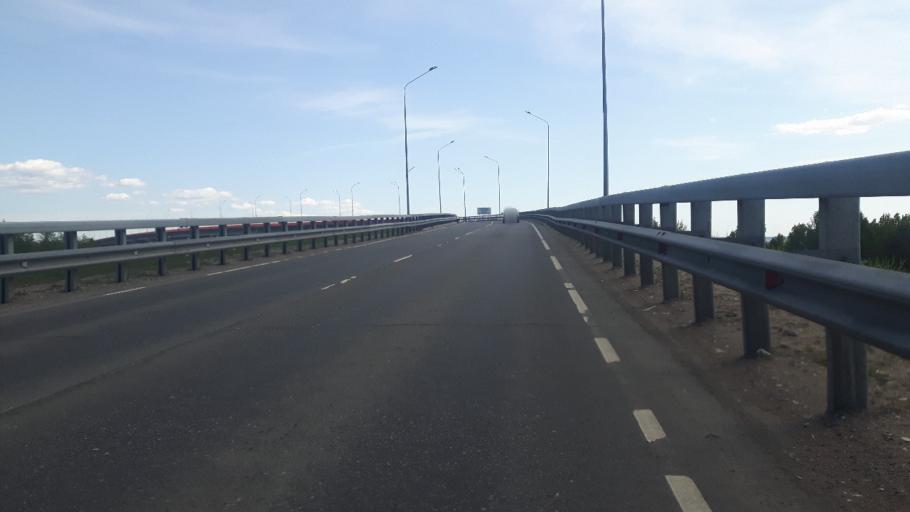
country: RU
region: Leningrad
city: Vyborg
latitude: 60.7402
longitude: 28.6837
